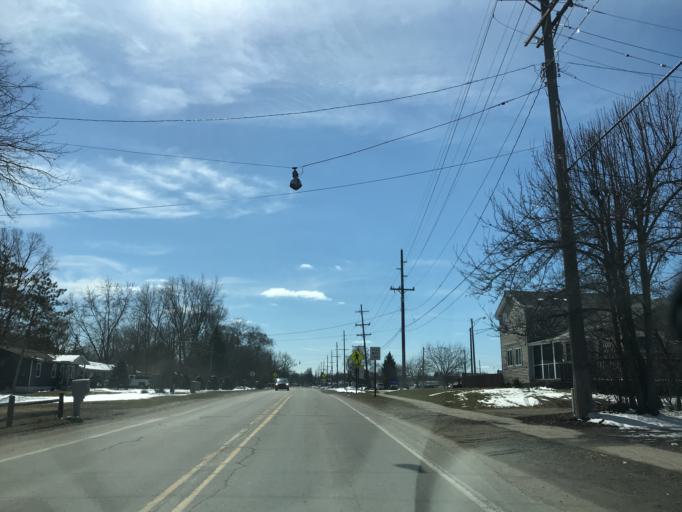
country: US
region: Michigan
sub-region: Livingston County
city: Whitmore Lake
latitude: 42.4151
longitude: -83.7611
